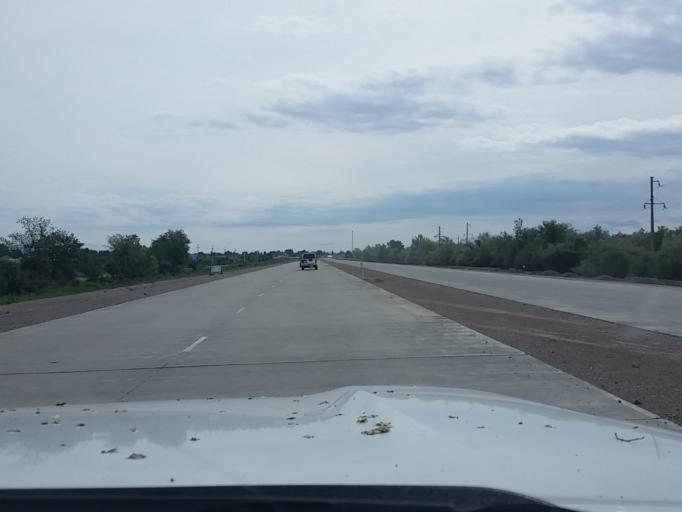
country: KZ
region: Almaty Oblysy
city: Turgen'
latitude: 43.5835
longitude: 78.2202
